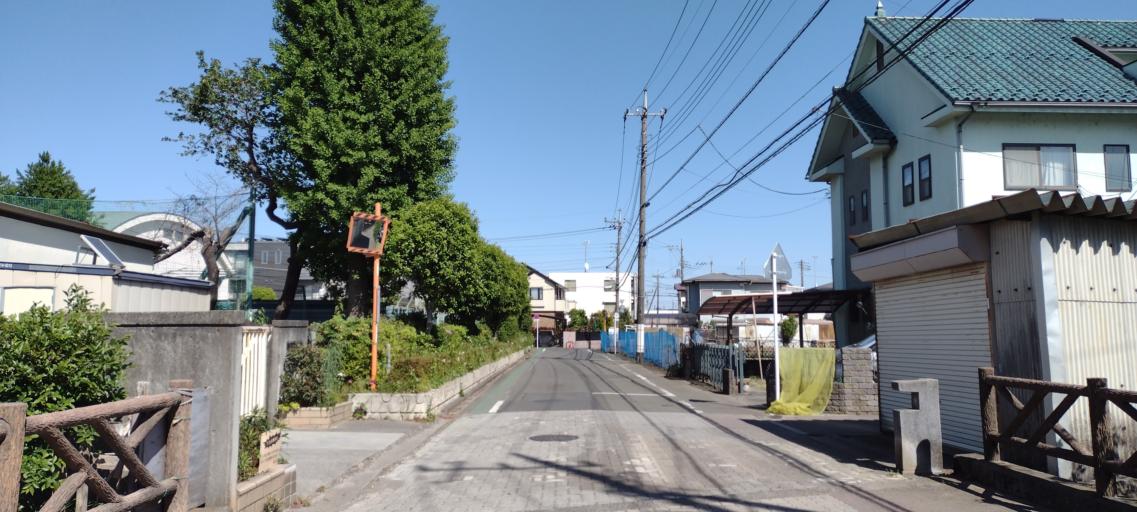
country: JP
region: Tokyo
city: Hino
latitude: 35.6843
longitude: 139.4276
